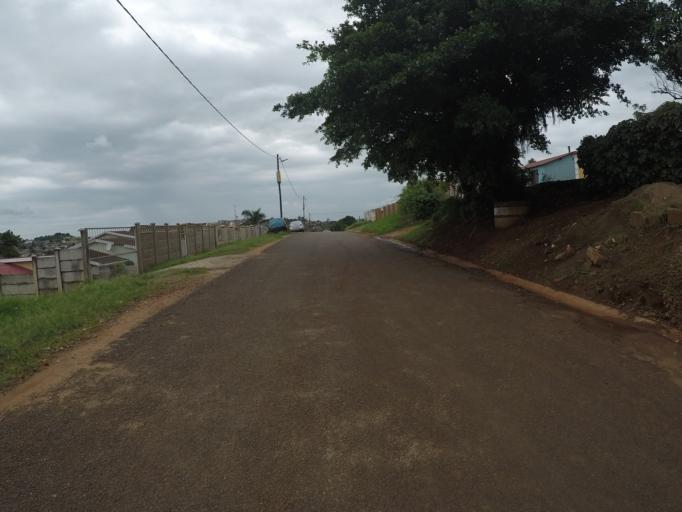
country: ZA
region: KwaZulu-Natal
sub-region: uThungulu District Municipality
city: Empangeni
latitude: -28.7769
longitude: 31.8627
